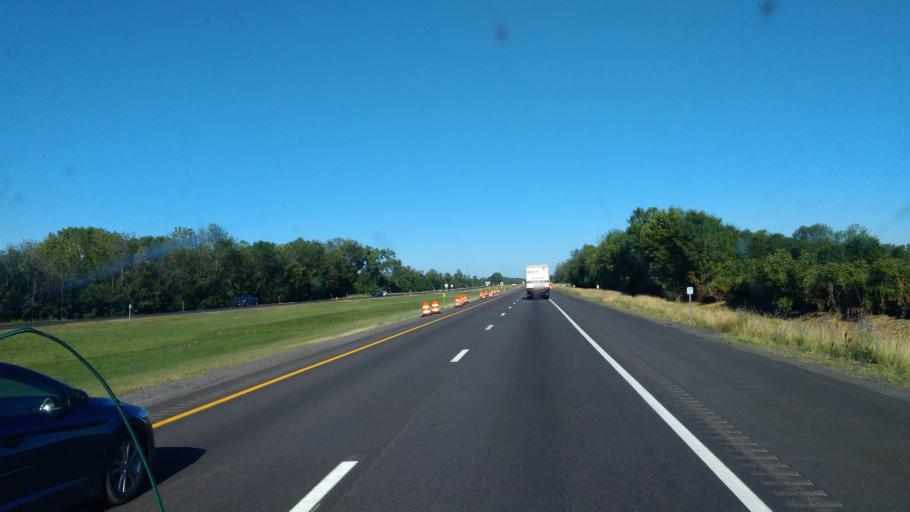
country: US
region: New York
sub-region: Ontario County
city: Clifton Springs
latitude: 42.9742
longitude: -77.1177
